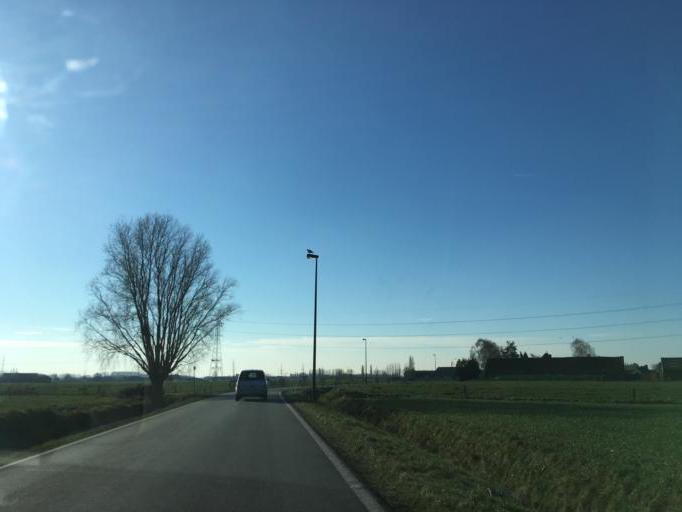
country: BE
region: Flanders
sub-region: Provincie Oost-Vlaanderen
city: Waarschoot
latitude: 51.1263
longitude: 3.5967
